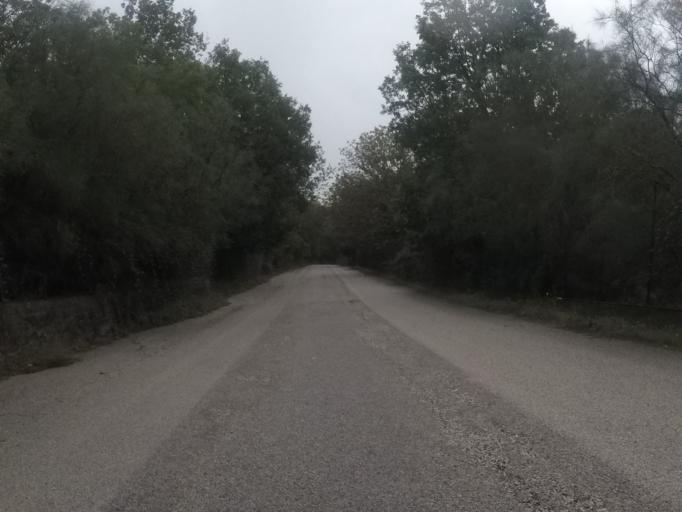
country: IT
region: Sicily
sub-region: Catania
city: Nicolosi
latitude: 37.6626
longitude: 15.0338
